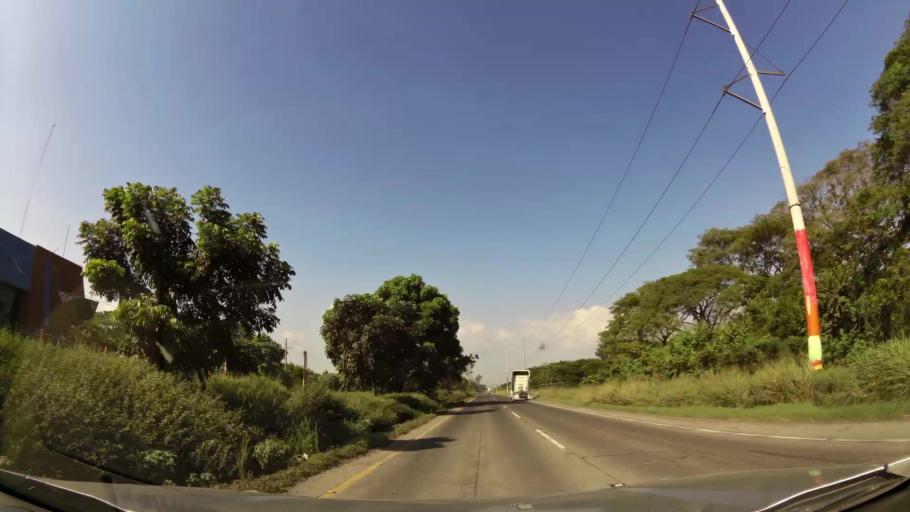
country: GT
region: Escuintla
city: Puerto San Jose
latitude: 13.9472
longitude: -90.7885
